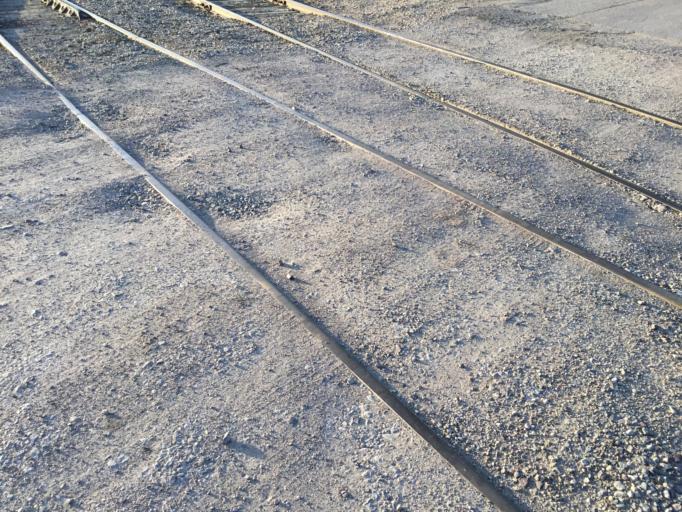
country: US
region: Kansas
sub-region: Mitchell County
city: Beloit
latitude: 39.4553
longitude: -98.1023
